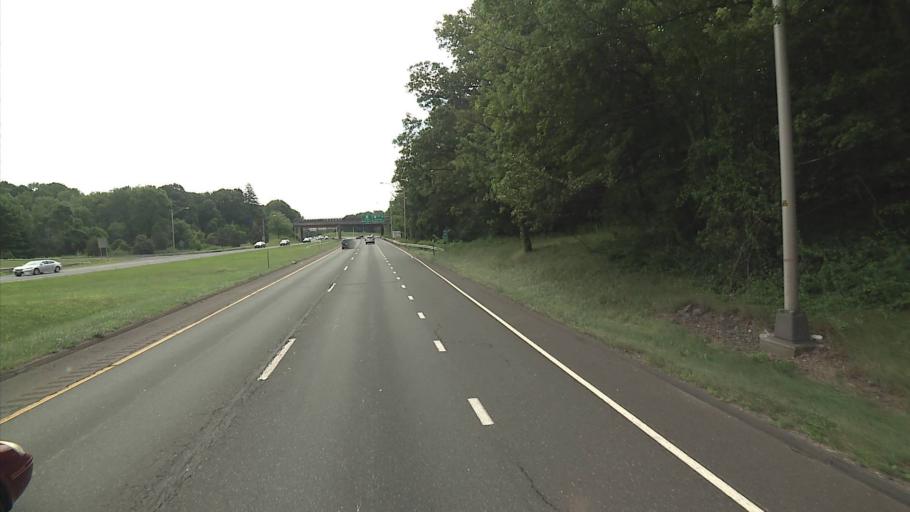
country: US
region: Connecticut
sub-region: Fairfield County
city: Newtown
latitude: 41.4188
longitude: -73.2930
